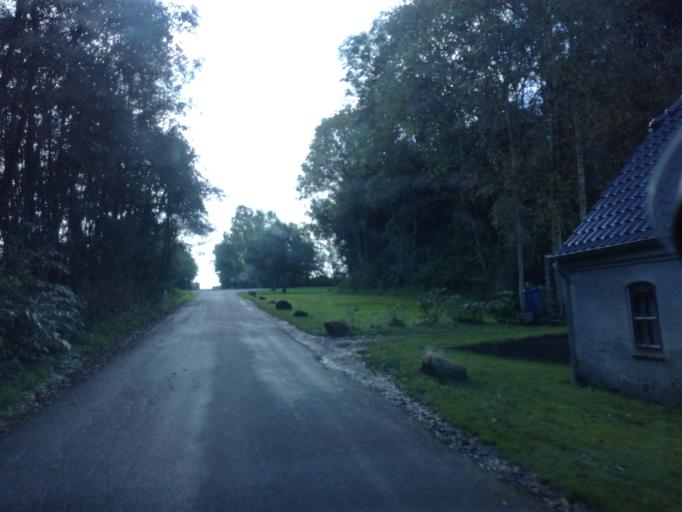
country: DK
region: South Denmark
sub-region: Vejle Kommune
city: Brejning
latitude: 55.6307
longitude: 9.7156
